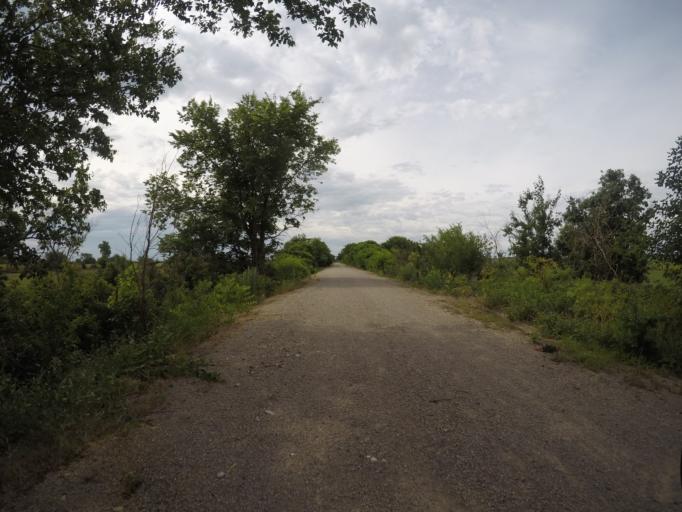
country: US
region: Kansas
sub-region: Anderson County
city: Garnett
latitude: 38.4268
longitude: -95.2633
